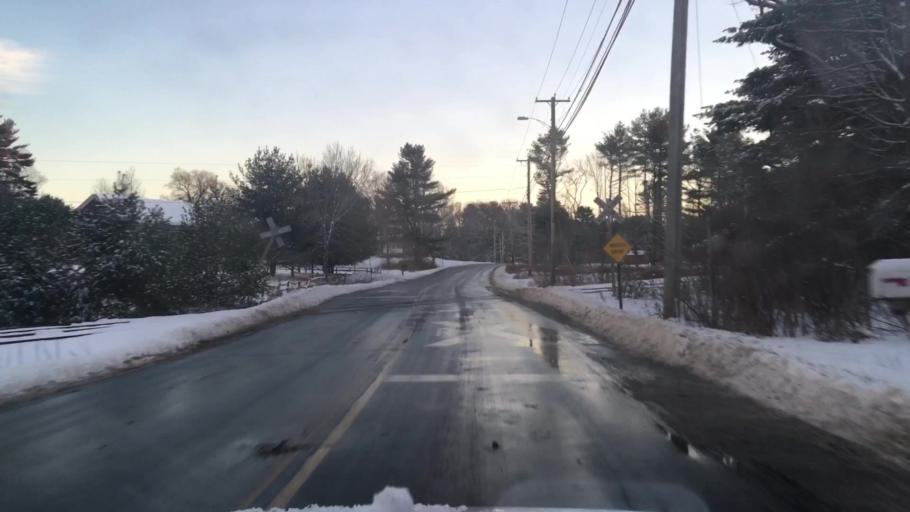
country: US
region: Maine
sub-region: Sagadahoc County
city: Topsham
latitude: 43.9586
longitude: -69.9287
